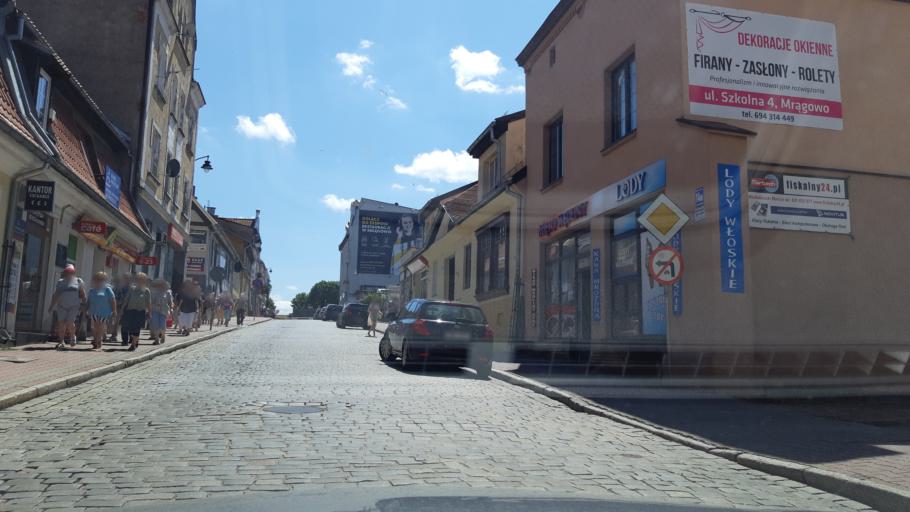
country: PL
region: Warmian-Masurian Voivodeship
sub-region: Powiat mragowski
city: Mragowo
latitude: 53.8683
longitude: 21.3052
